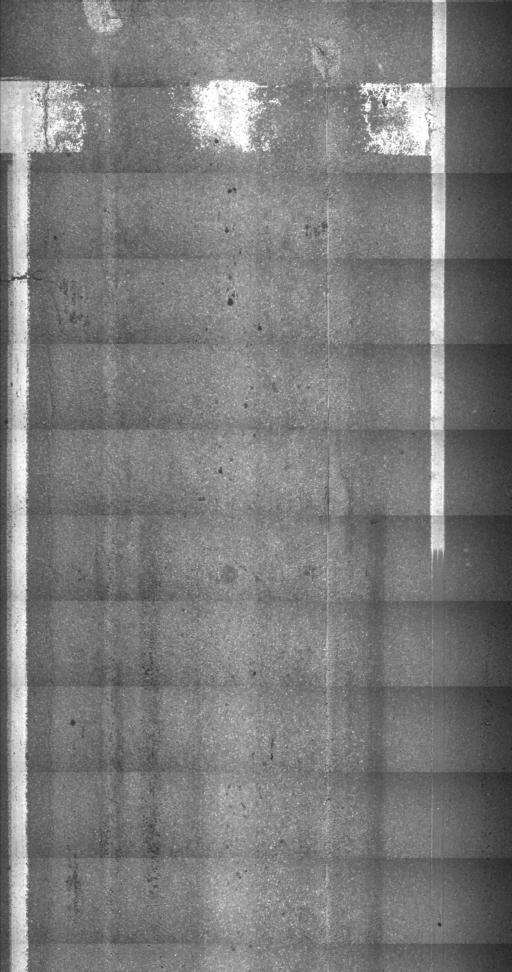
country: US
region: Vermont
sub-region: Chittenden County
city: Williston
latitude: 44.4483
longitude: -73.1079
